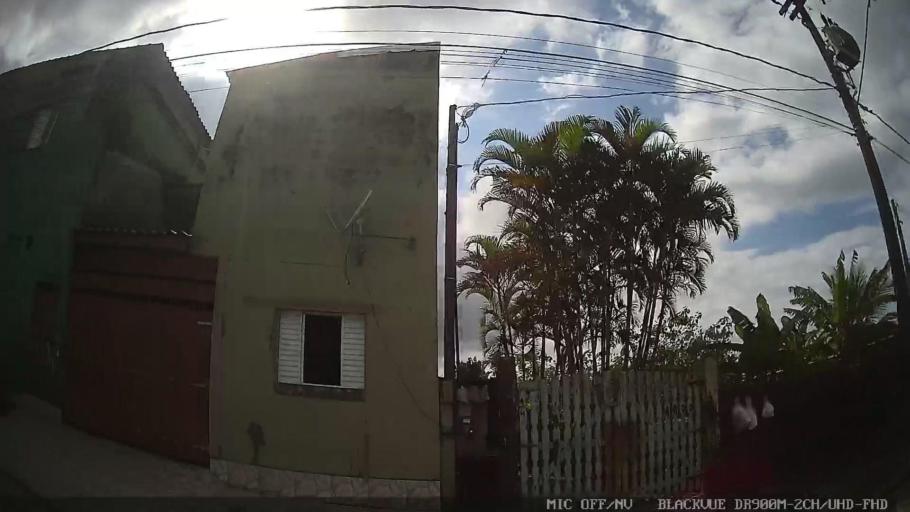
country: BR
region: Sao Paulo
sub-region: Itanhaem
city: Itanhaem
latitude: -24.1974
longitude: -46.8397
